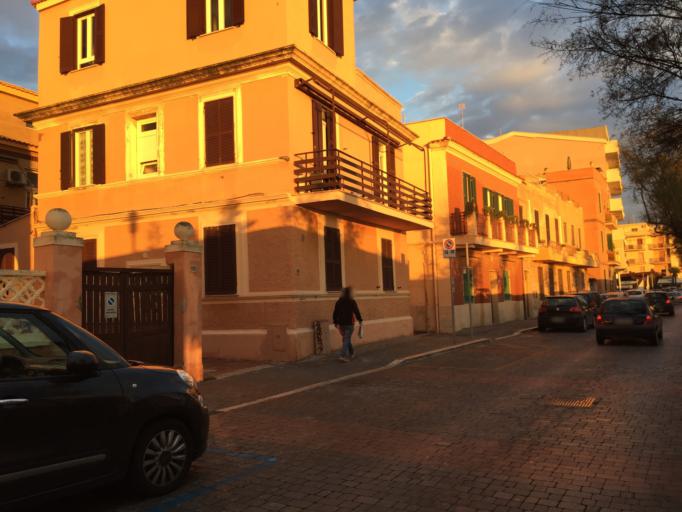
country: IT
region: Latium
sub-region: Citta metropolitana di Roma Capitale
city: Ladispoli
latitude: 41.9481
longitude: 12.0756
